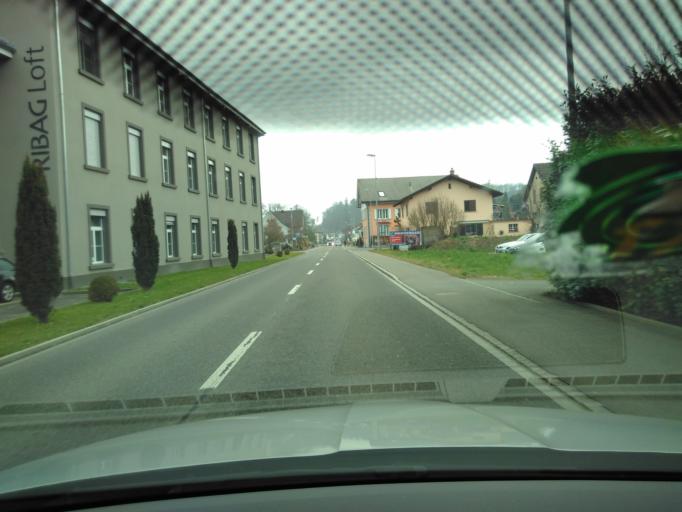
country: CH
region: Aargau
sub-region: Bezirk Aarau
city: Muhen
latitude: 47.3278
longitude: 8.0557
